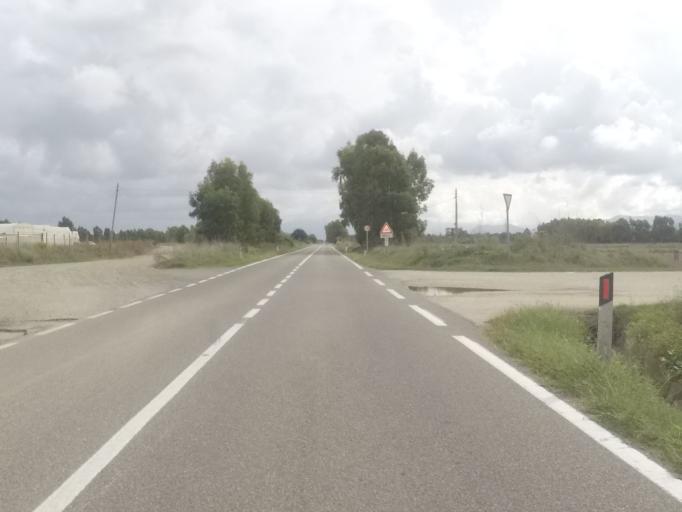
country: IT
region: Sardinia
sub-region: Provincia di Oristano
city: San Nicolo d'Arcidano
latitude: 39.6560
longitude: 8.6535
